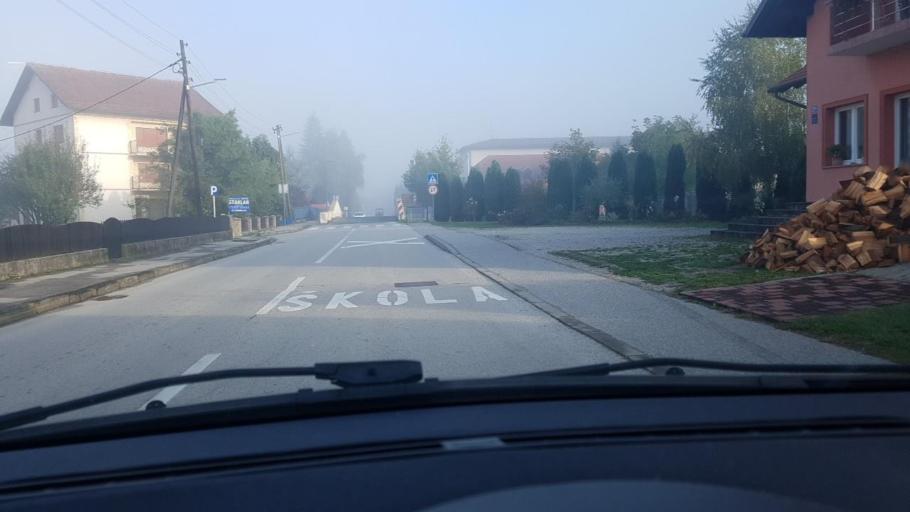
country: HR
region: Krapinsko-Zagorska
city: Marija Bistrica
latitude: 46.0007
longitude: 16.1197
